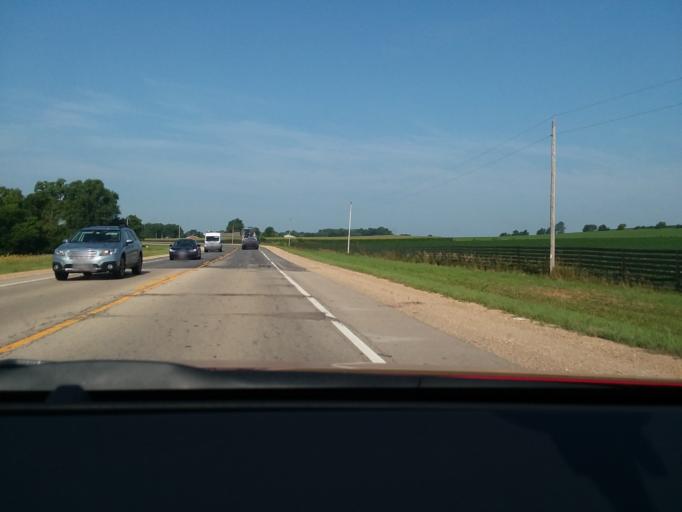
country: US
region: Wisconsin
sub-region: Dane County
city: Windsor
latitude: 43.1959
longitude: -89.3789
